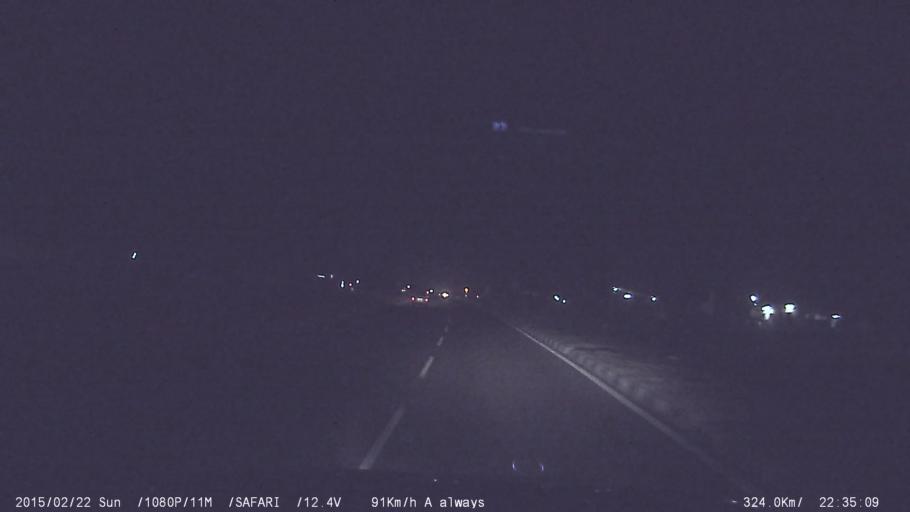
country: IN
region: Tamil Nadu
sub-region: Namakkal
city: Velur
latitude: 11.1296
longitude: 78.0174
